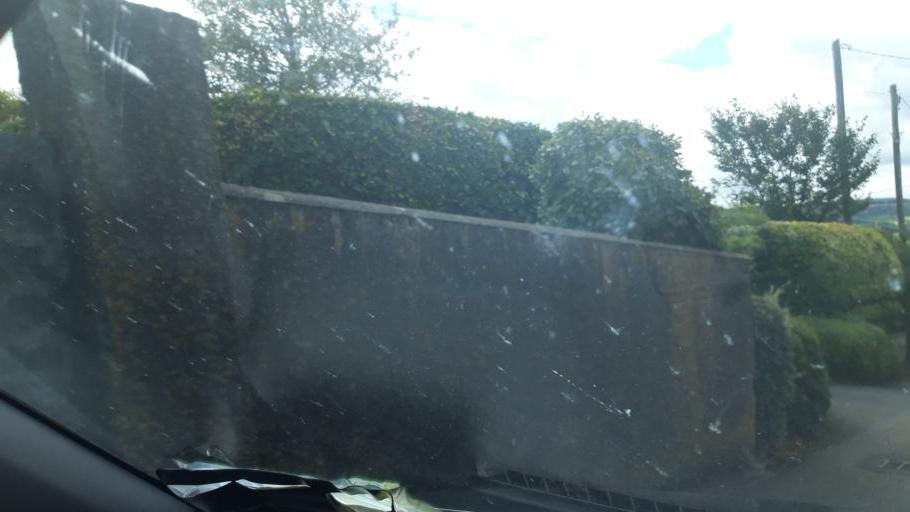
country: IE
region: Munster
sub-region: South Tipperary
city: Cluain Meala
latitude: 52.3585
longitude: -7.6876
